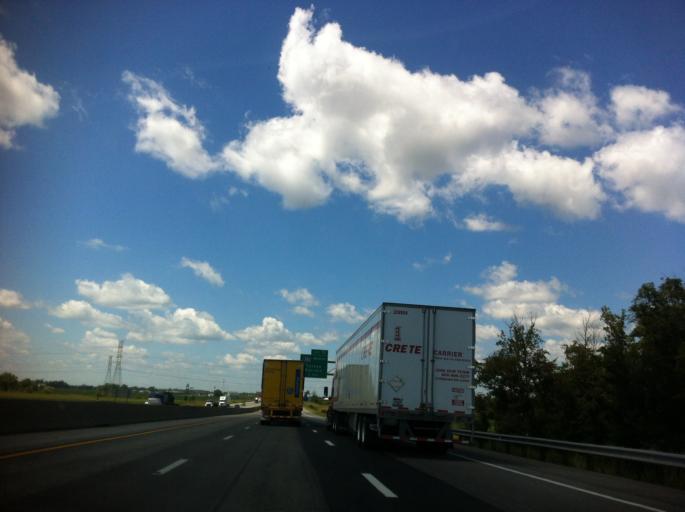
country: US
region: Ohio
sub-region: Wood County
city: Millbury
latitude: 41.5164
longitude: -83.4377
